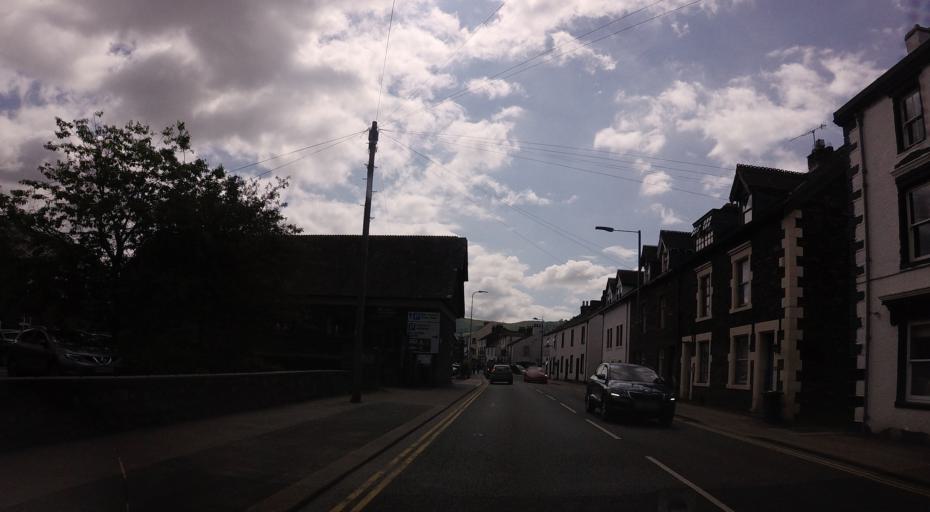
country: GB
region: England
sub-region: Cumbria
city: Keswick
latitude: 54.6027
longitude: -3.1413
